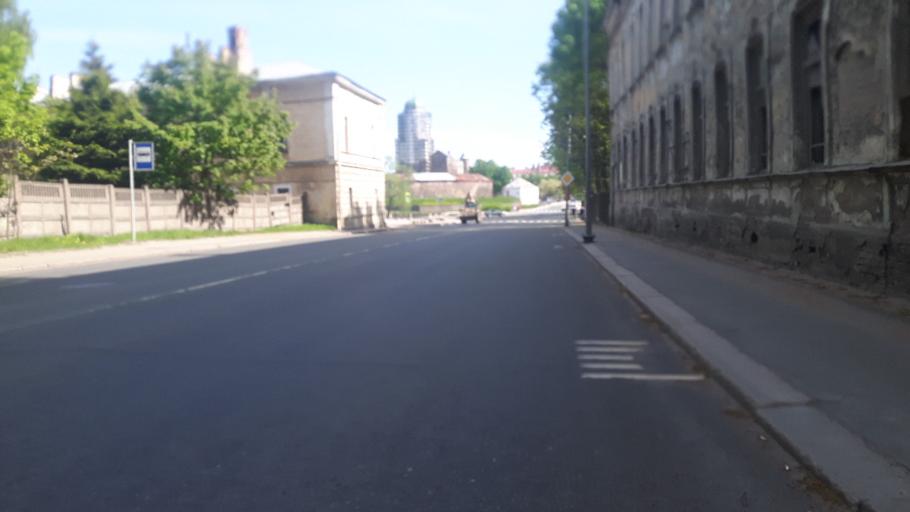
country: RU
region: Leningrad
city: Vyborg
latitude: 60.7179
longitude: 28.7228
